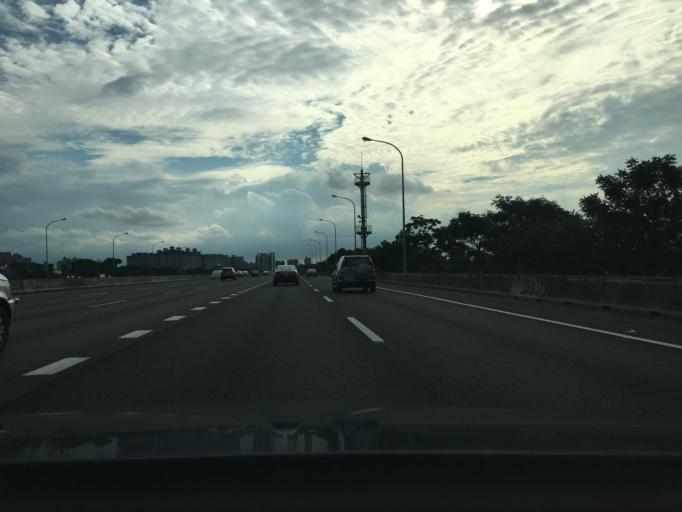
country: TW
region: Taiwan
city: Taoyuan City
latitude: 24.9749
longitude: 121.2220
